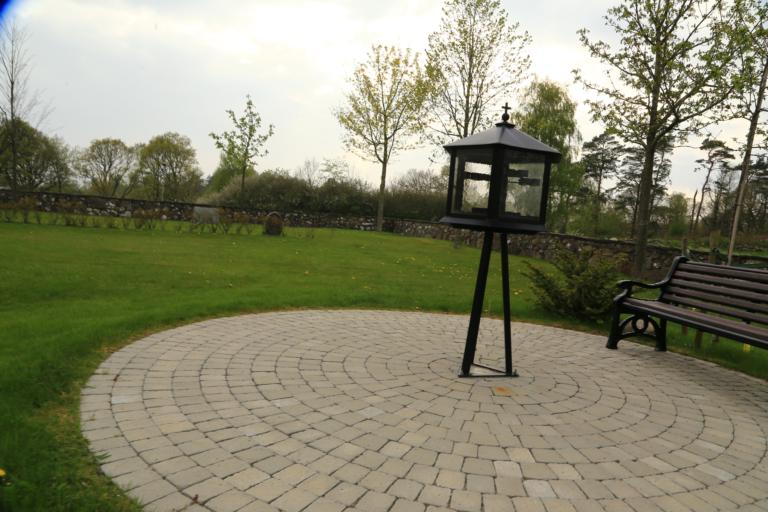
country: SE
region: Halland
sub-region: Varbergs Kommun
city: Tvaaker
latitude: 57.1335
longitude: 12.3821
